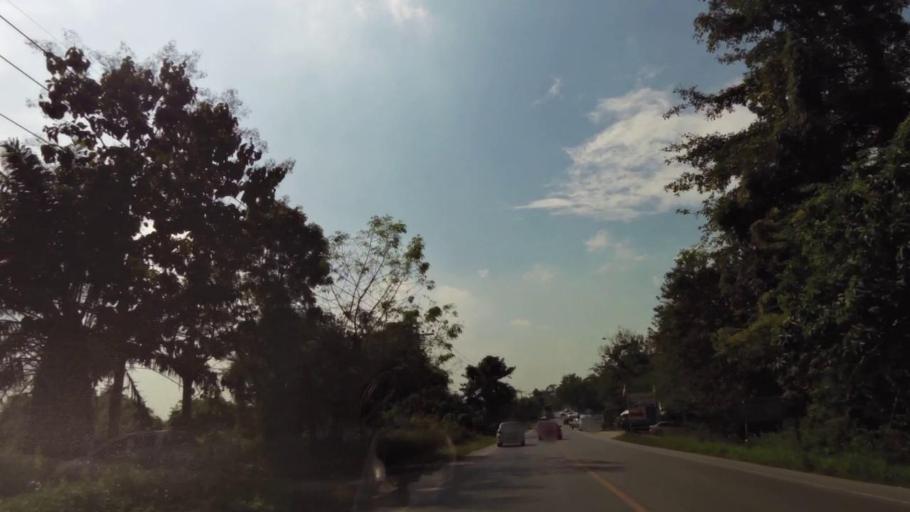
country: TH
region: Chiang Rai
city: Chiang Rai
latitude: 19.8652
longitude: 99.7739
